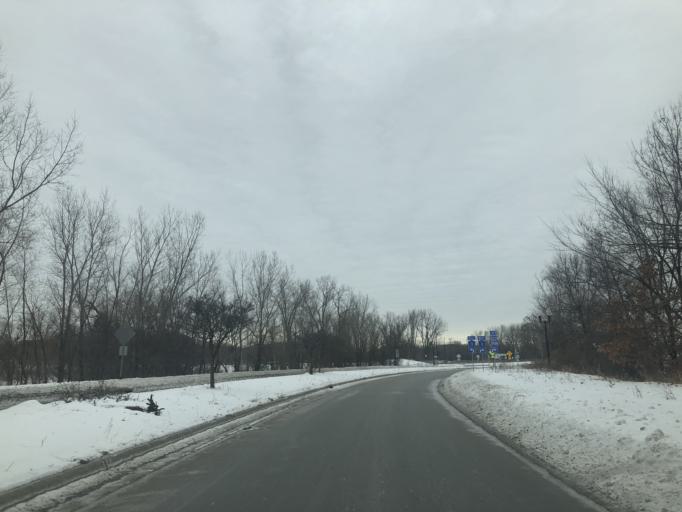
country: US
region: Minnesota
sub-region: Ramsey County
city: Mounds View
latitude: 45.1095
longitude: -93.1871
